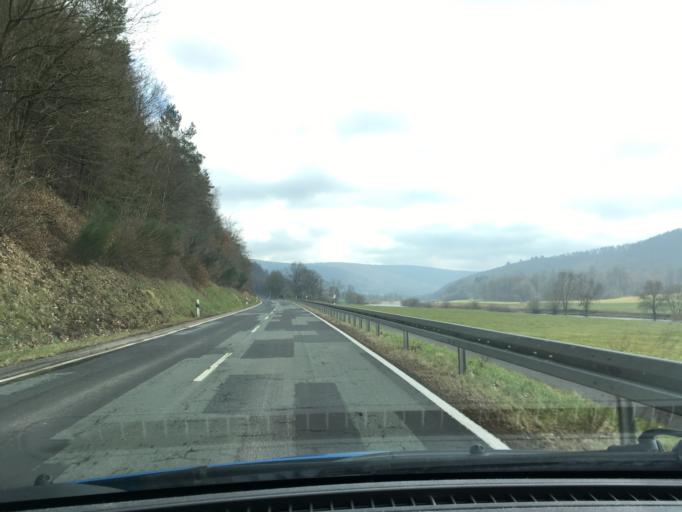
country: DE
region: Lower Saxony
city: Bodenfelde
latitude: 51.5629
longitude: 9.6053
